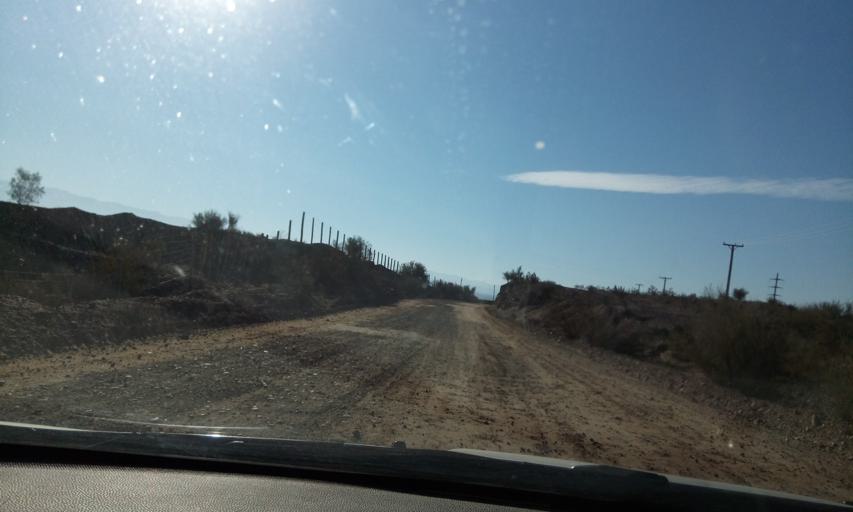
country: AR
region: San Juan
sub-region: Departamento de Rivadavia
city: Rivadavia
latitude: -31.4183
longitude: -68.6706
